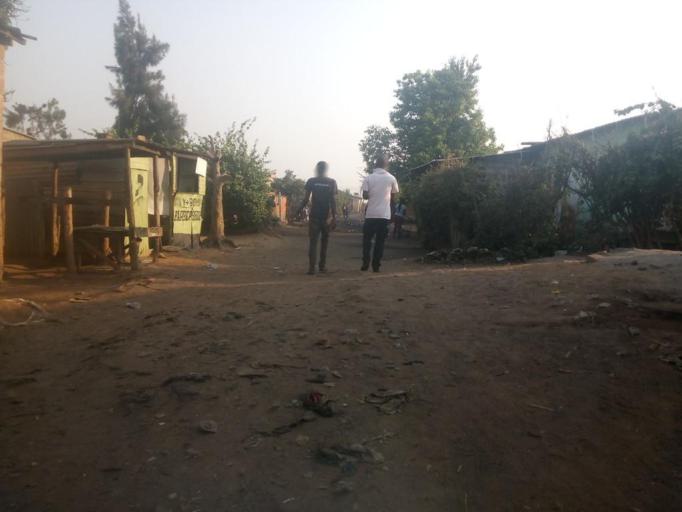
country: ZM
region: Lusaka
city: Lusaka
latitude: -15.4077
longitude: 28.3628
